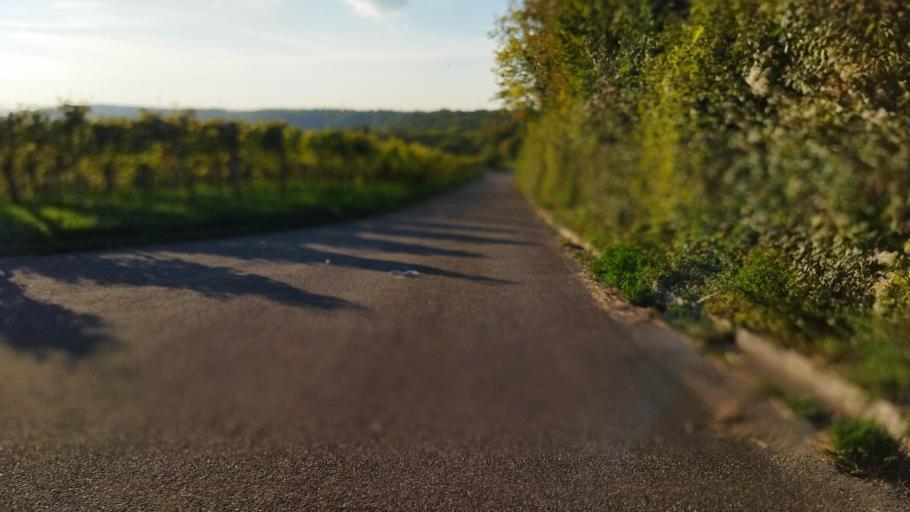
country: DE
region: Baden-Wuerttemberg
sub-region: Regierungsbezirk Stuttgart
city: Grossbottwar
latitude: 49.0288
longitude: 9.2738
